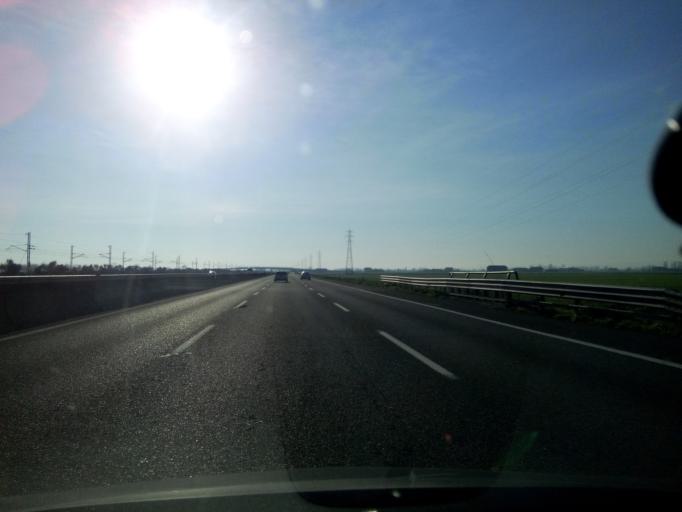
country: IT
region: Emilia-Romagna
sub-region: Provincia di Reggio Emilia
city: Prato
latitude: 44.7069
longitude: 10.7310
